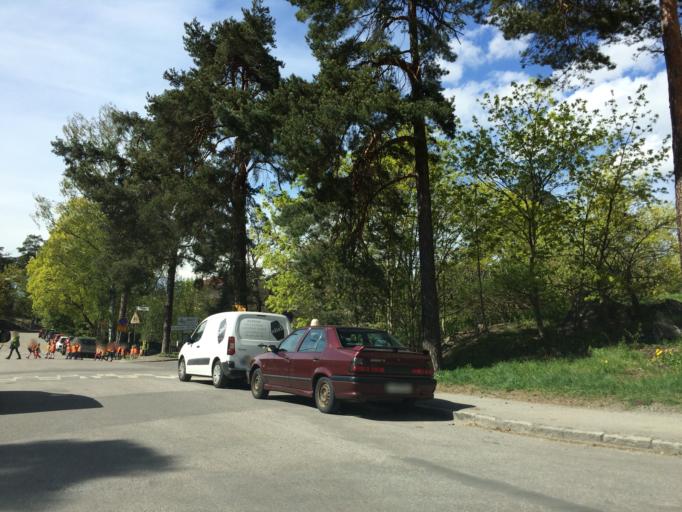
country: SE
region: Stockholm
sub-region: Huddinge Kommun
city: Segeltorp
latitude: 59.3041
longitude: 17.9597
